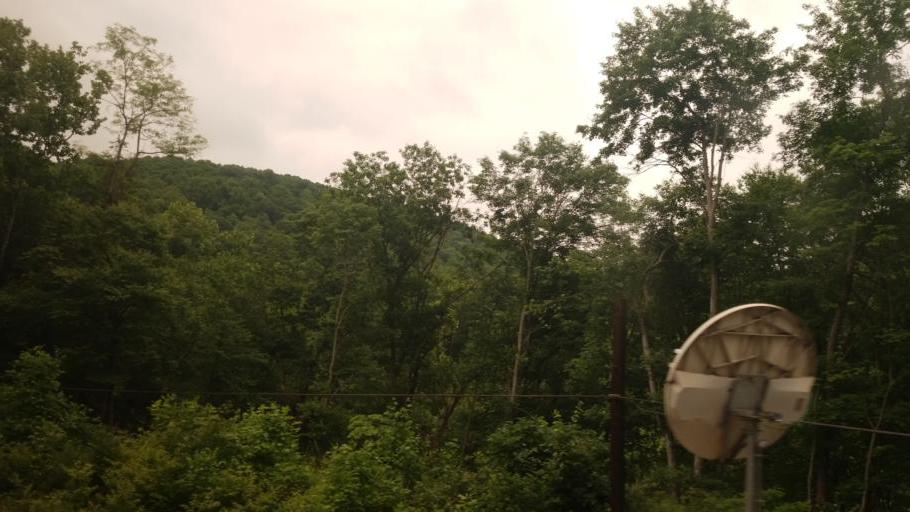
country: US
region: Pennsylvania
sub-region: Fayette County
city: South Connellsville
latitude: 39.9058
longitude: -79.4874
